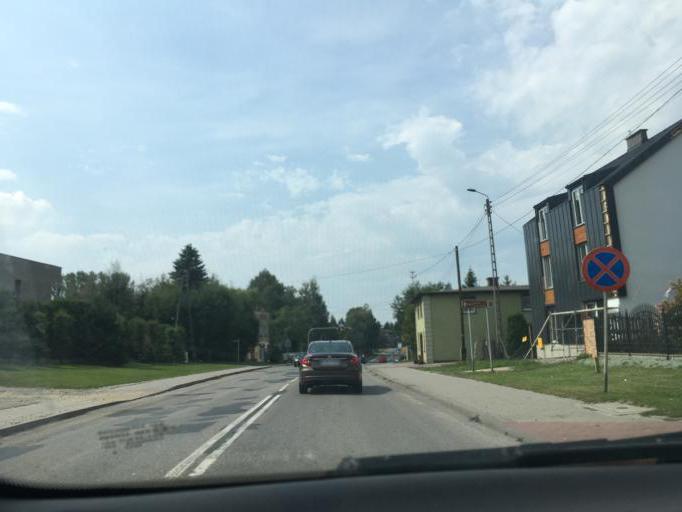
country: PL
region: Silesian Voivodeship
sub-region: Powiat rybnicki
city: Belk
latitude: 50.1306
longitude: 18.7121
